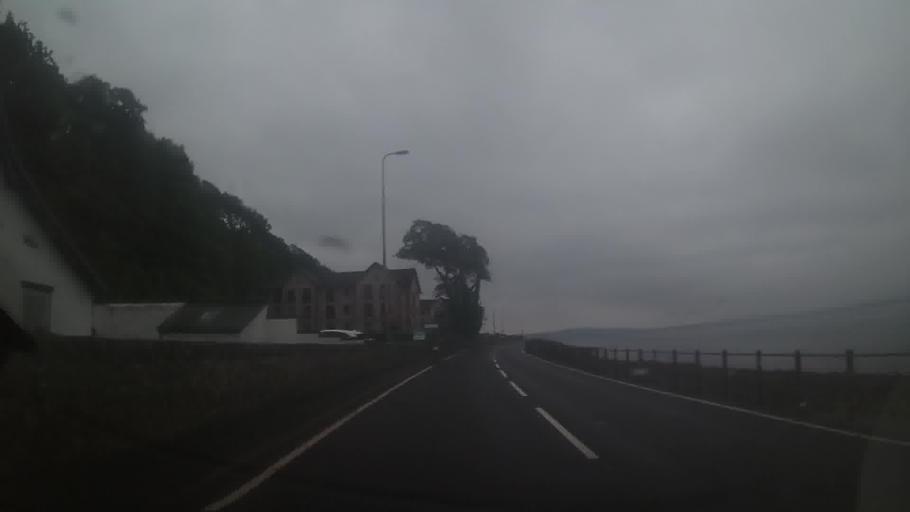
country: GB
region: Scotland
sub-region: North Ayrshire
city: Skelmorlie
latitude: 55.8599
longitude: -4.8895
